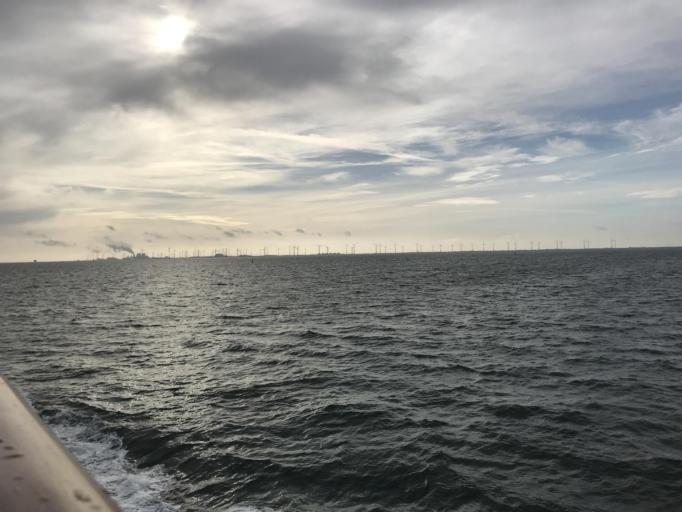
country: DE
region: Lower Saxony
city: Borkum
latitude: 53.5243
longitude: 6.7695
